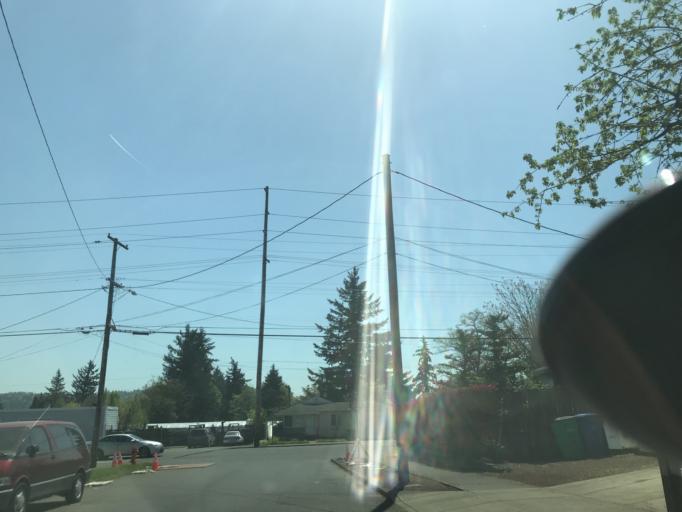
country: US
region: Oregon
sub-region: Multnomah County
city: Lents
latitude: 45.4902
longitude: -122.5584
